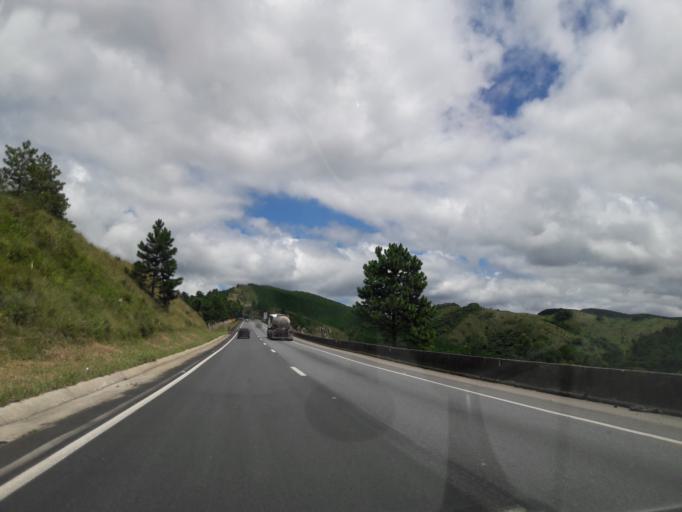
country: BR
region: Parana
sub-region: Campina Grande Do Sul
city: Campina Grande do Sul
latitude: -25.1010
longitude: -48.8280
